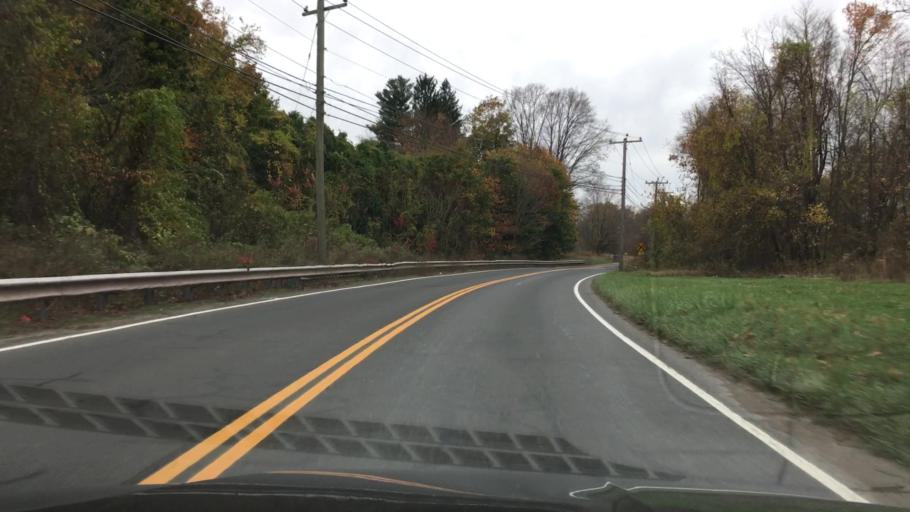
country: US
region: Connecticut
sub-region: Hartford County
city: Hazardville
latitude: 41.9715
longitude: -72.5149
